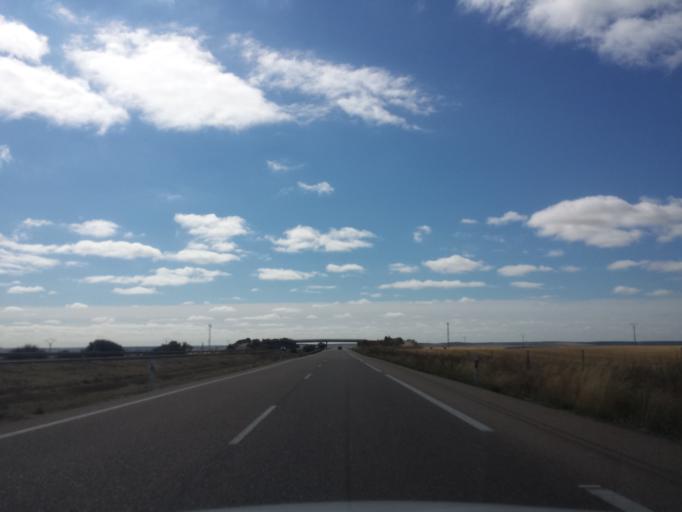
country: ES
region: Castille and Leon
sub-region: Provincia de Zamora
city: Cerecinos de Campos
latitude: 41.8851
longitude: -5.4610
